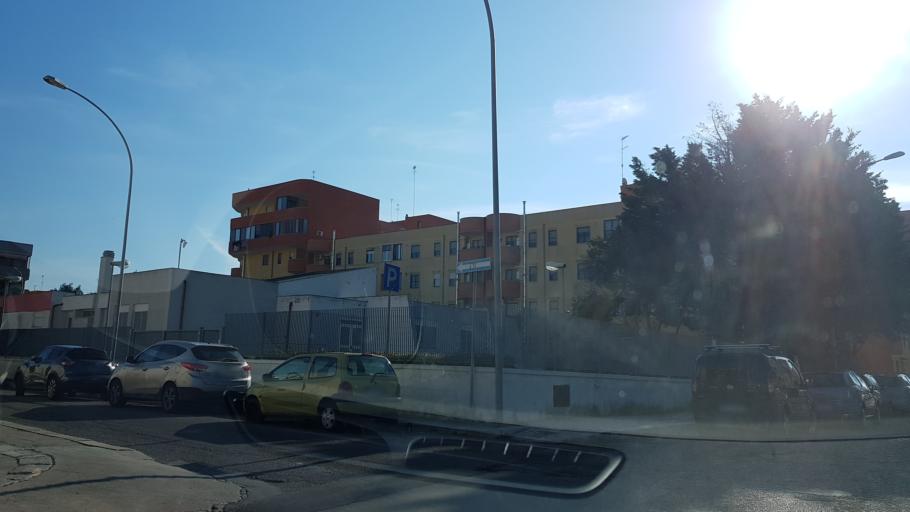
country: IT
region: Apulia
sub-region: Provincia di Brindisi
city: Brindisi
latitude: 40.6223
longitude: 17.9310
